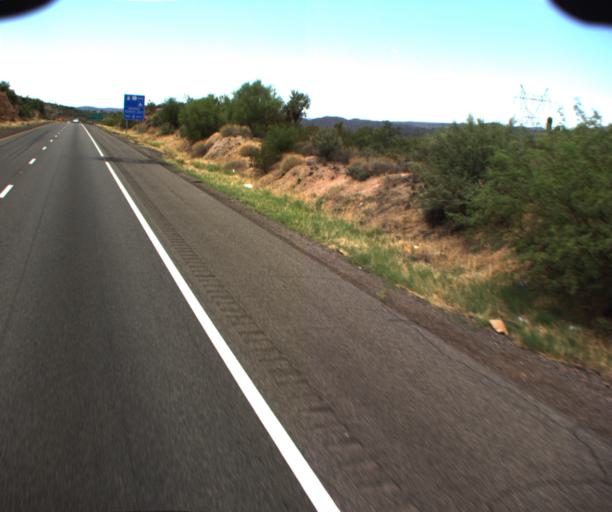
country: US
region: Arizona
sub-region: Yavapai County
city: Black Canyon City
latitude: 34.0988
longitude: -112.1430
